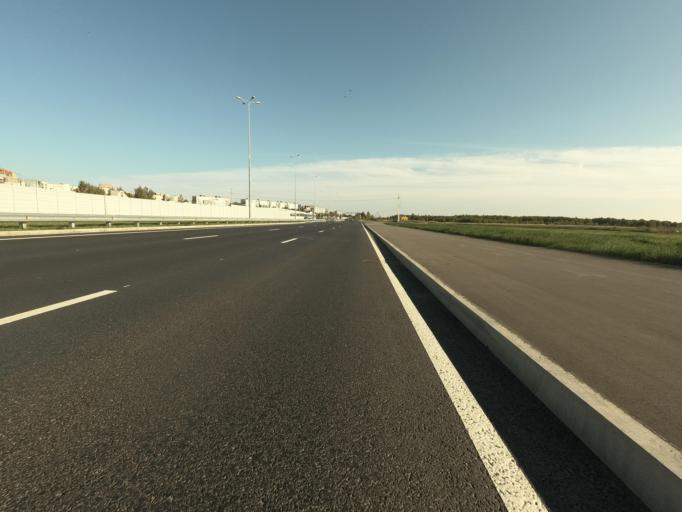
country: RU
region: St.-Petersburg
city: Kolpino
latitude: 59.7383
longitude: 30.5526
